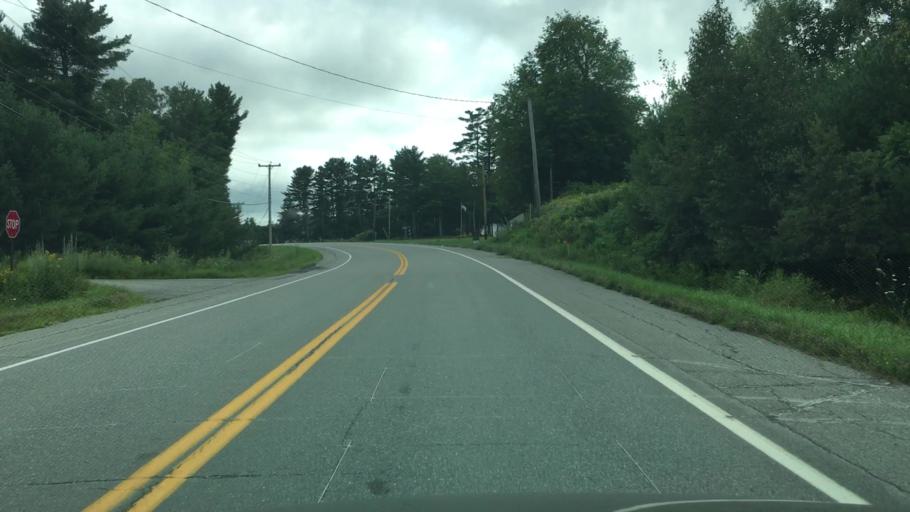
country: US
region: Maine
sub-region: Waldo County
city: Frankfort
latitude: 44.6228
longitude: -68.8698
